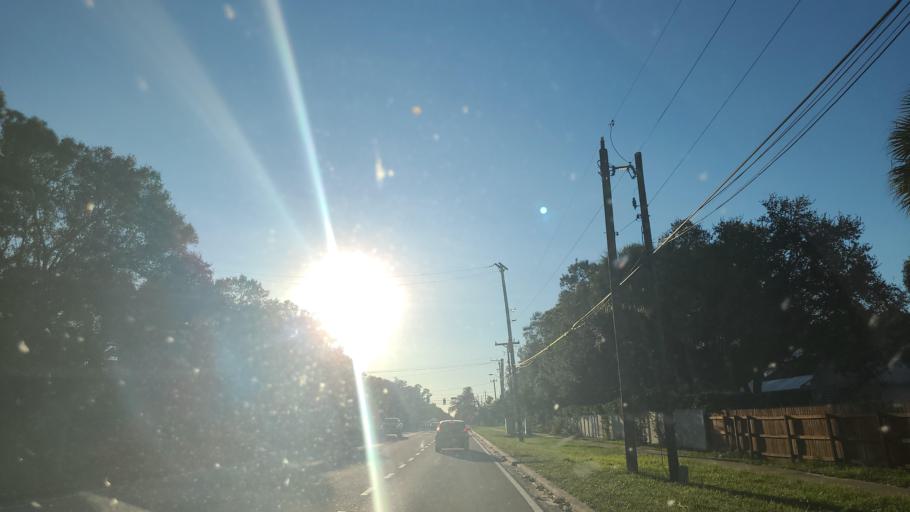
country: US
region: Florida
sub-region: Indian River County
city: Vero Beach South
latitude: 27.6090
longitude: -80.4292
